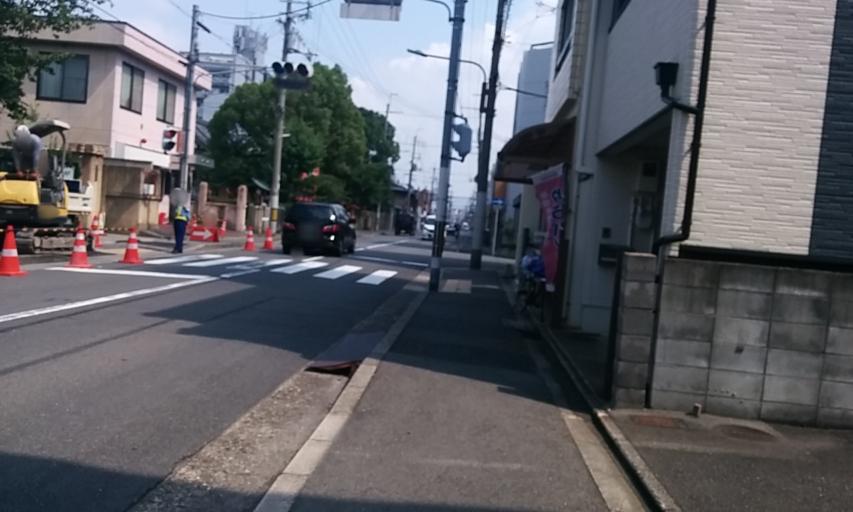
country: JP
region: Kyoto
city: Kyoto
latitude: 34.9876
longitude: 135.7364
